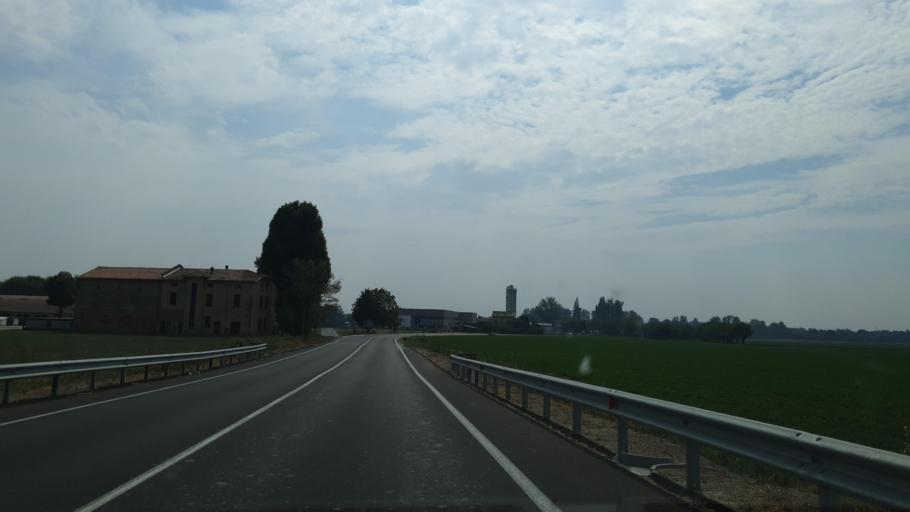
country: IT
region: Emilia-Romagna
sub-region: Provincia di Parma
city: San Secondo Parmense
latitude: 44.8837
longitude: 10.2562
